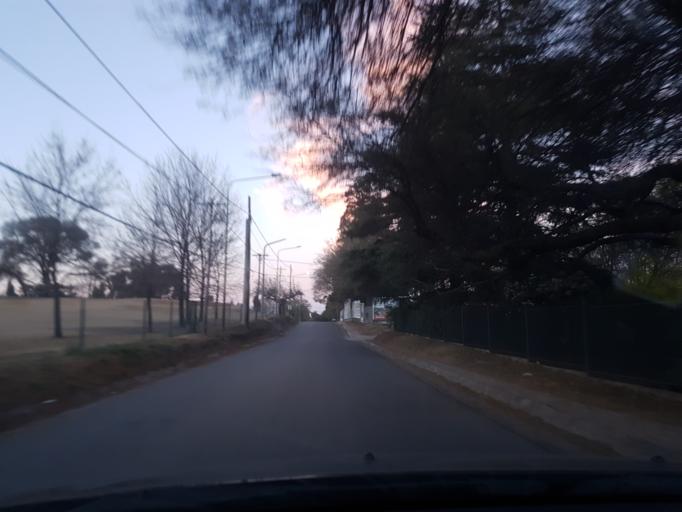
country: AR
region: Cordoba
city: Villa Allende
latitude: -31.2837
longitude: -64.2905
